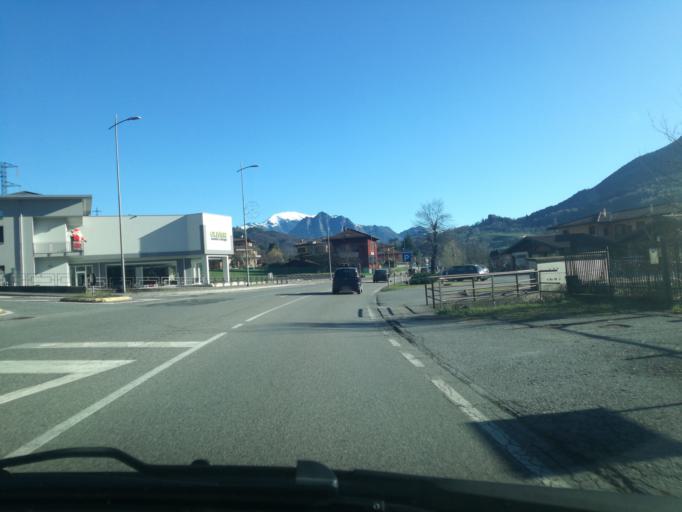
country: IT
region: Lombardy
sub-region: Provincia di Bergamo
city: Piangaiano
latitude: 45.7902
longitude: 9.9884
